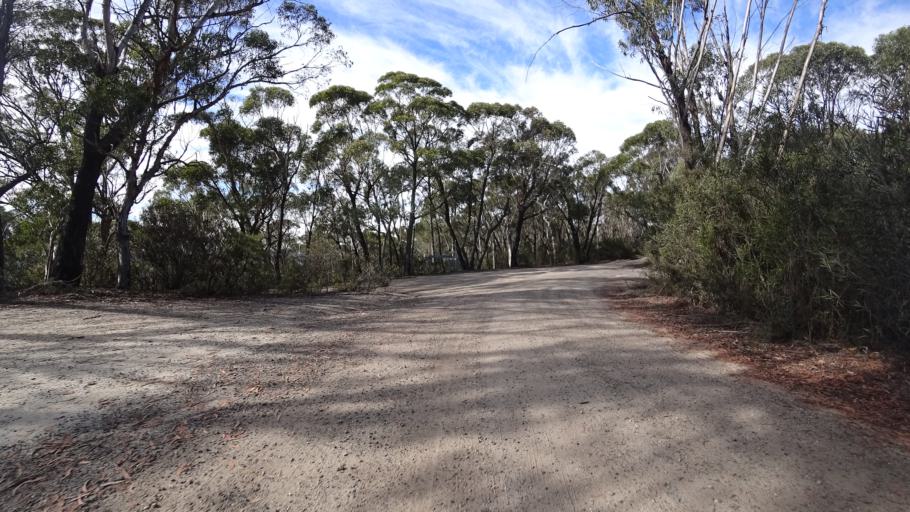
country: AU
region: New South Wales
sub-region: Lithgow
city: Lithgow
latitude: -33.5046
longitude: 150.1642
